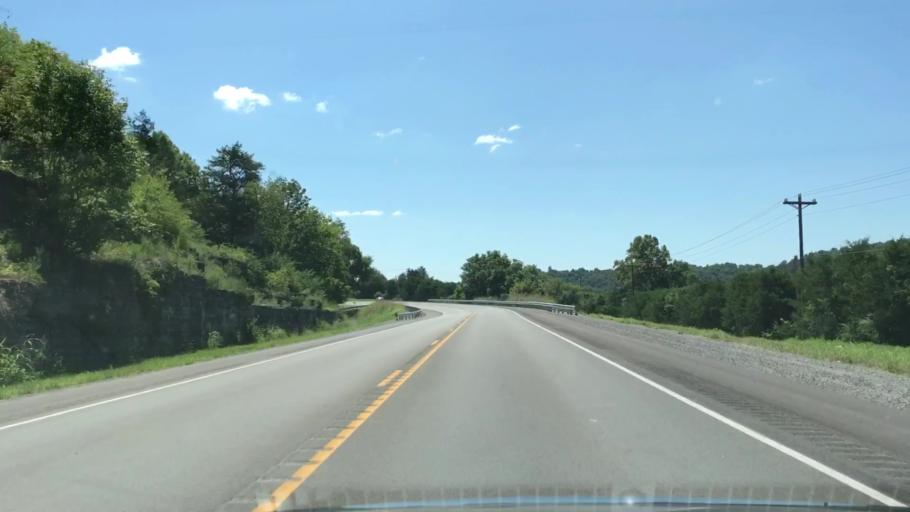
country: US
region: Kentucky
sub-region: Cumberland County
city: Burkesville
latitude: 36.7601
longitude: -85.3787
